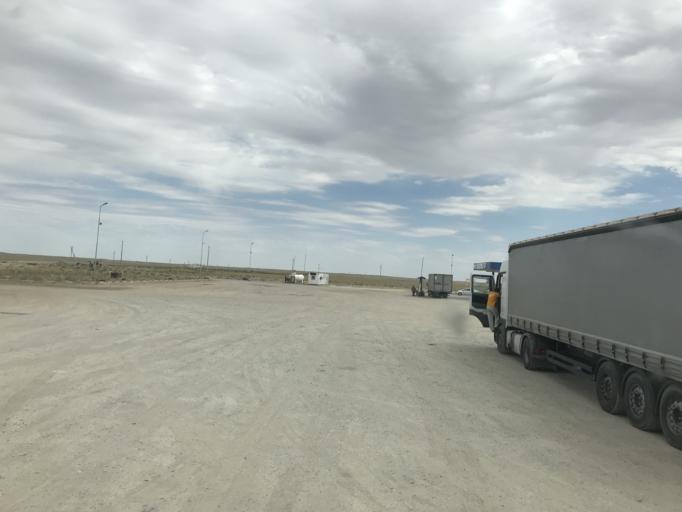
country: KZ
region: Qyzylorda
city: Aral
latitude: 46.8288
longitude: 61.6910
